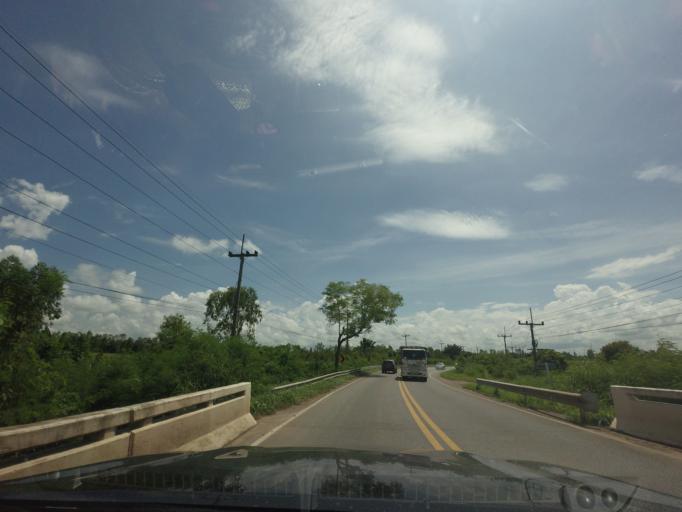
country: TH
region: Changwat Udon Thani
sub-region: Amphoe Ban Phue
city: Ban Phue
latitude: 17.7150
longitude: 102.4110
